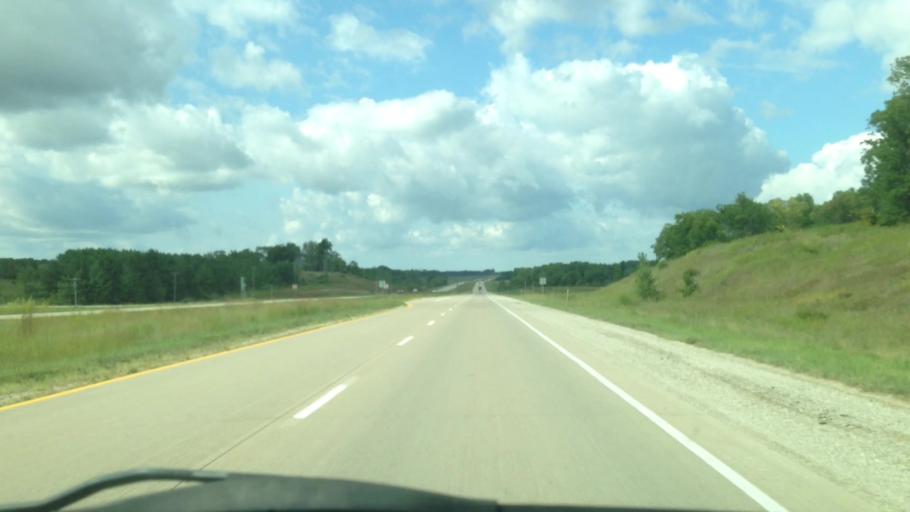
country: US
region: Illinois
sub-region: Hancock County
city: Nauvoo
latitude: 40.5522
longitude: -91.5650
